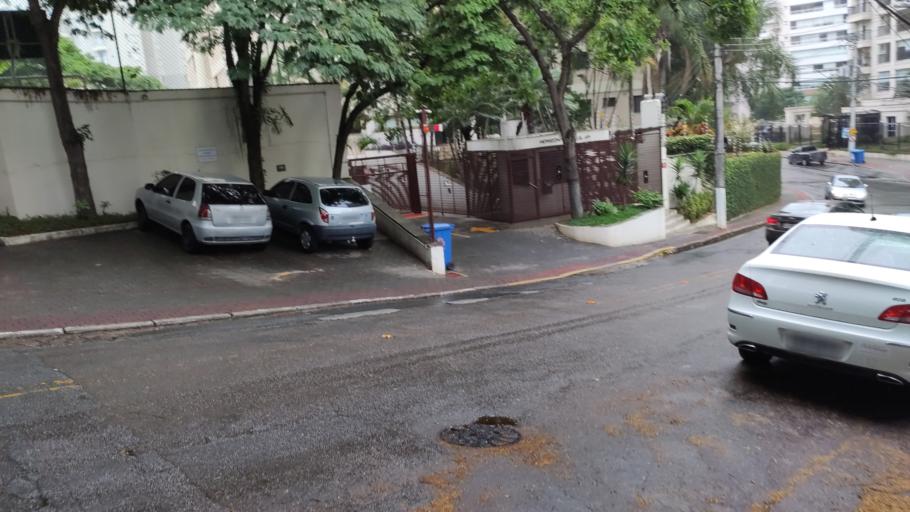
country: BR
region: Sao Paulo
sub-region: Sao Jose Dos Campos
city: Sao Jose dos Campos
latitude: -23.2072
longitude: -45.9019
